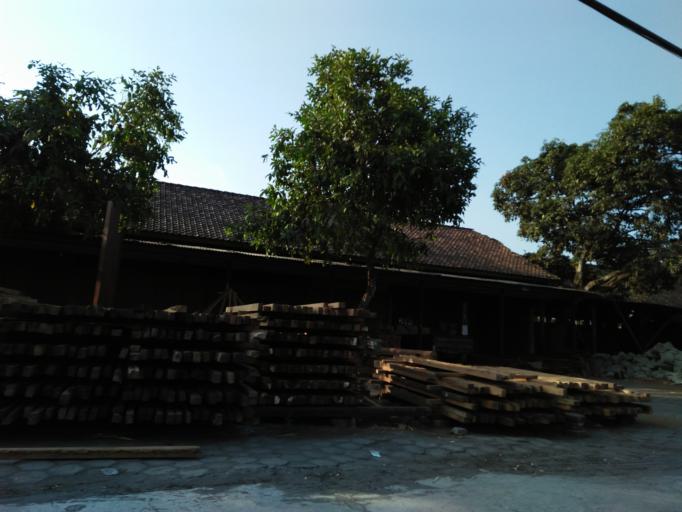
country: ID
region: Daerah Istimewa Yogyakarta
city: Depok
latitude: -7.7753
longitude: 110.4622
